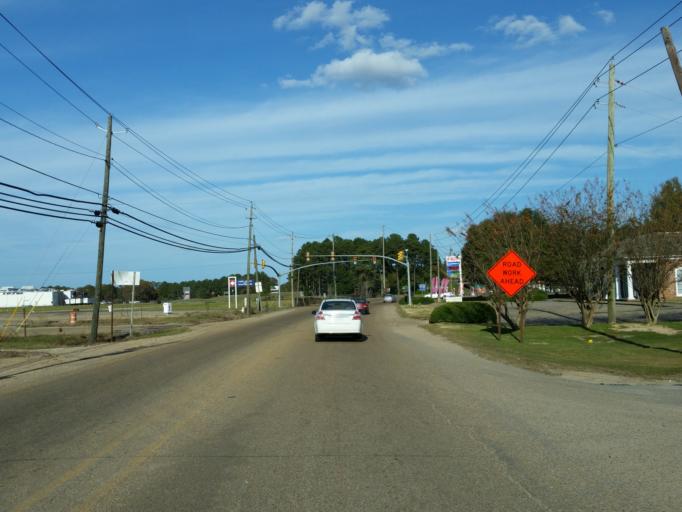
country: US
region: Mississippi
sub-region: Jones County
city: Laurel
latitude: 31.6623
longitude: -89.1622
